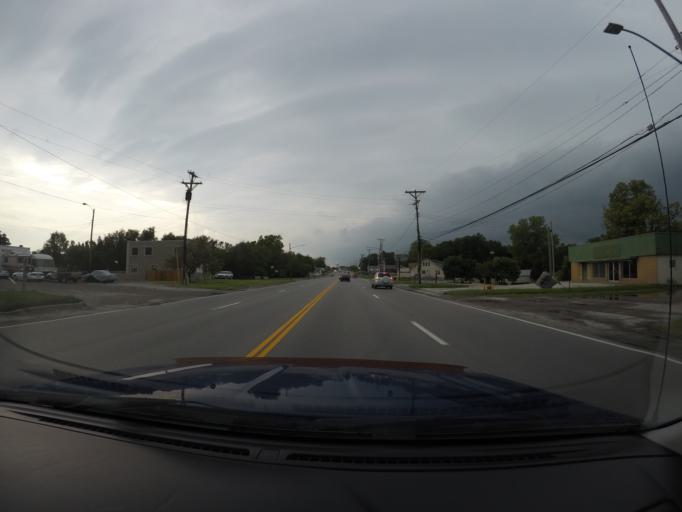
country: US
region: Missouri
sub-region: Jackson County
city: Independence
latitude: 39.1028
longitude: -94.3986
